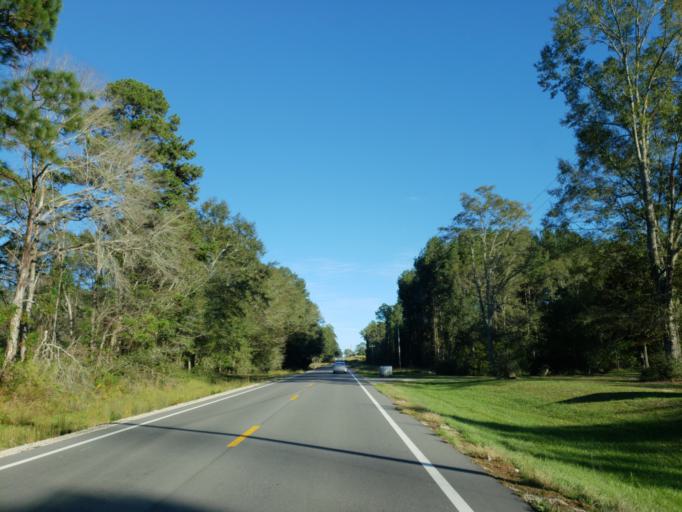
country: US
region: Mississippi
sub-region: Perry County
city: Richton
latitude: 31.3622
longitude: -89.0464
